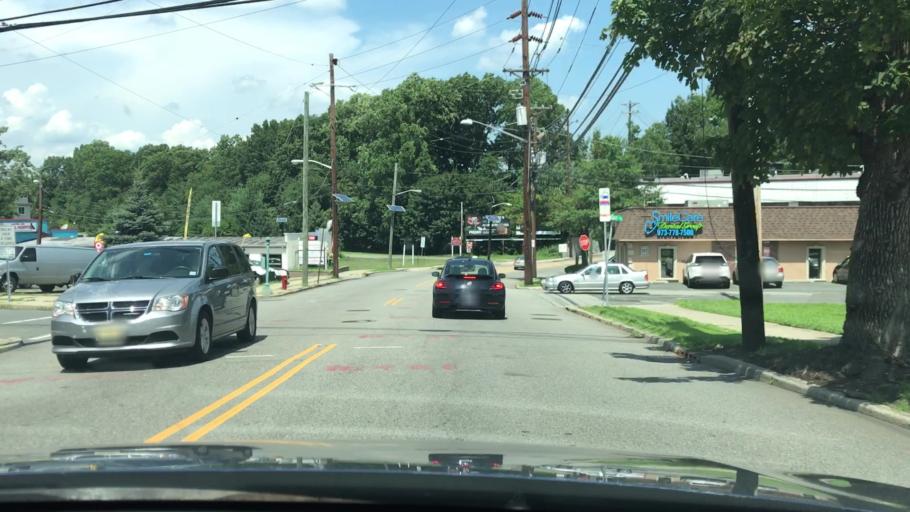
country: US
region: New Jersey
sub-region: Passaic County
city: Clifton
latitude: 40.8688
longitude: -74.1556
